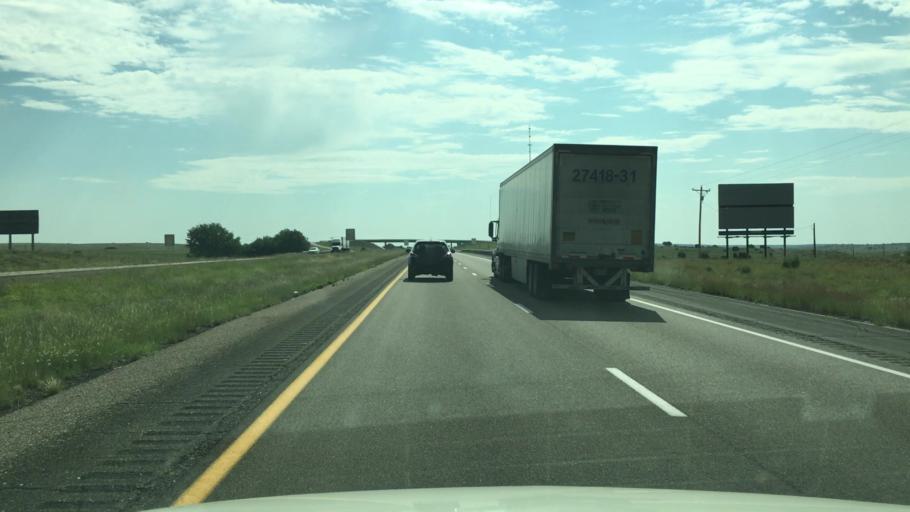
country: US
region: New Mexico
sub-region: San Miguel County
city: Las Vegas
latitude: 34.9918
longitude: -105.3014
